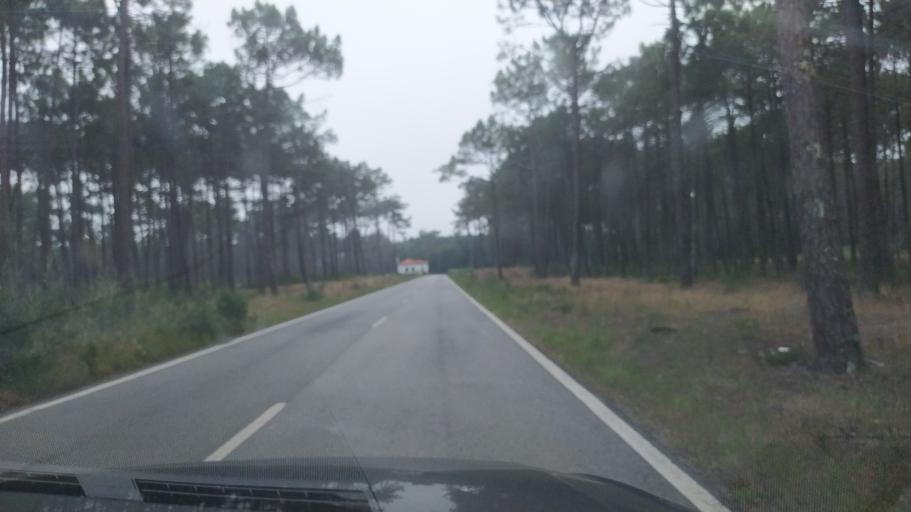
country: PT
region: Aveiro
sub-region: Ilhavo
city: Gafanha da Encarnacao
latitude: 40.5804
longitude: -8.7332
